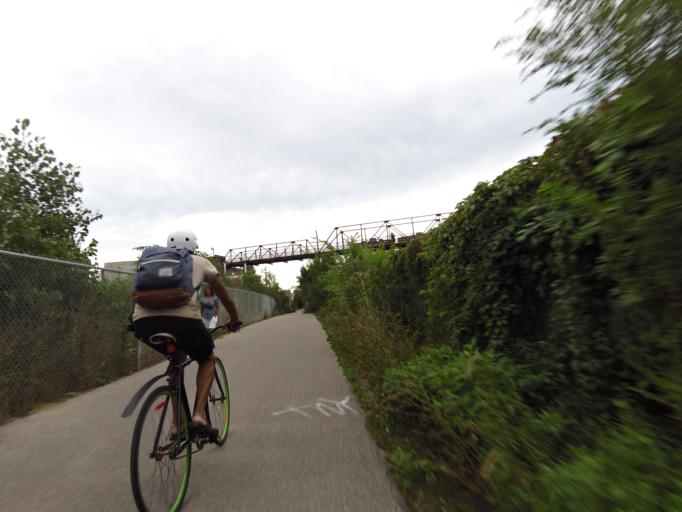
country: CA
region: Ontario
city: Toronto
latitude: 43.6609
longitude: -79.4536
